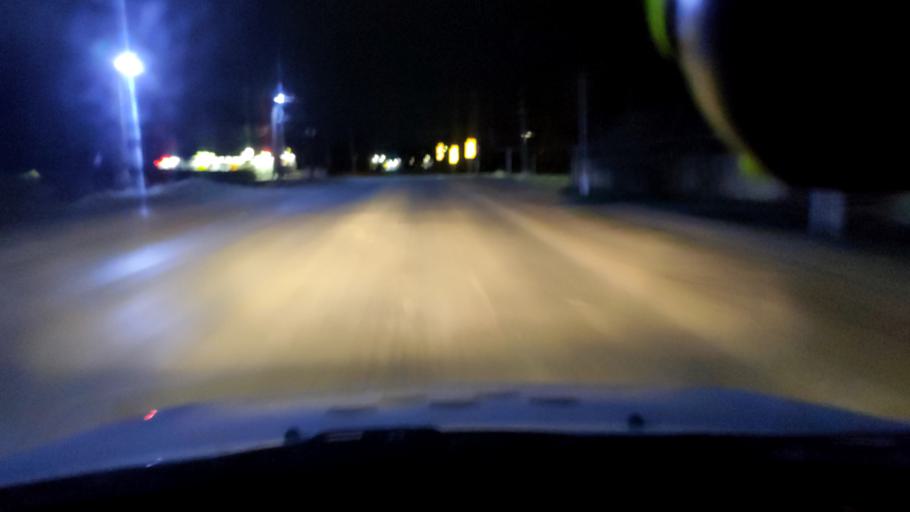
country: RU
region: Samara
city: Podstepki
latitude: 53.6019
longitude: 49.0413
